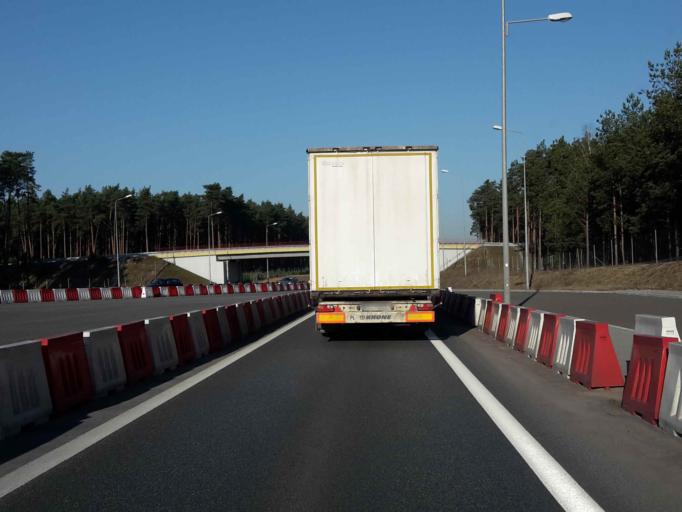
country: PL
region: Kujawsko-Pomorskie
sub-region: Torun
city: Torun
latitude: 52.9685
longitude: 18.6679
